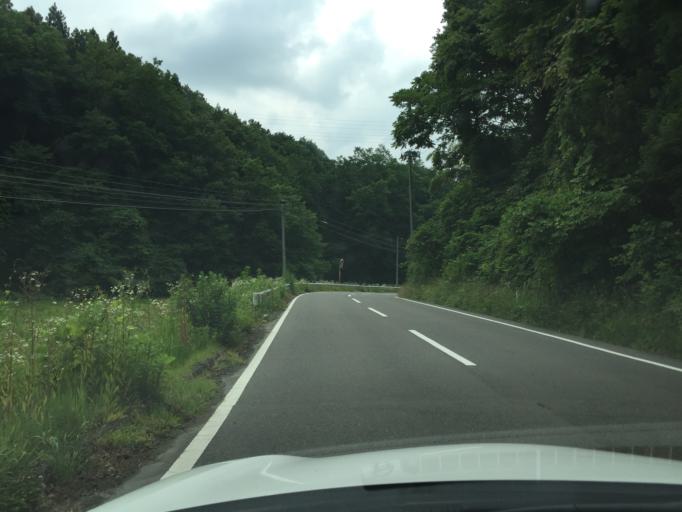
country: JP
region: Fukushima
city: Ishikawa
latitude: 37.2051
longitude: 140.4679
